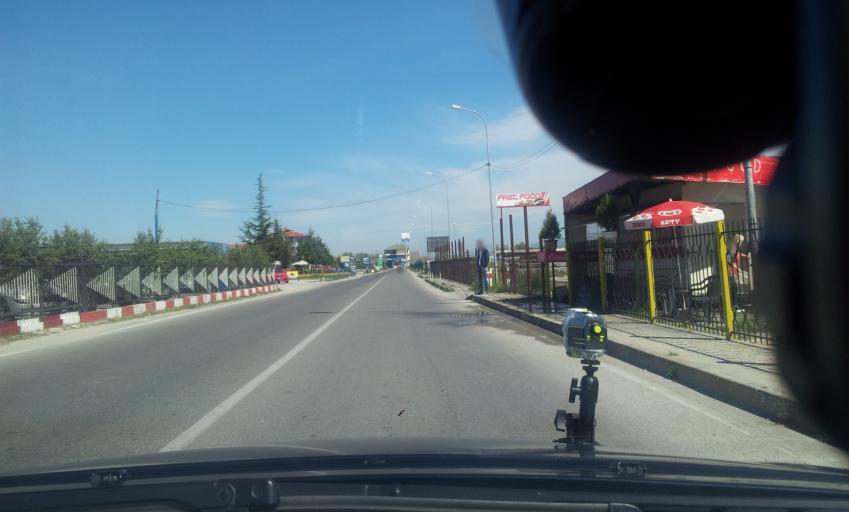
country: AL
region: Tirane
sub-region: Rrethi i Tiranes
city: Preze
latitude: 41.4219
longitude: 19.7129
